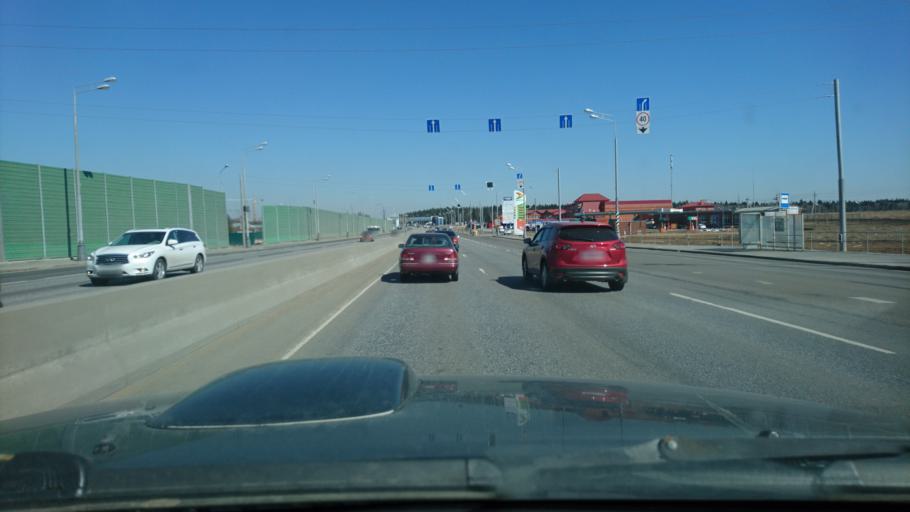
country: RU
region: Moskovskaya
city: Filimonki
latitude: 55.5228
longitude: 37.3840
